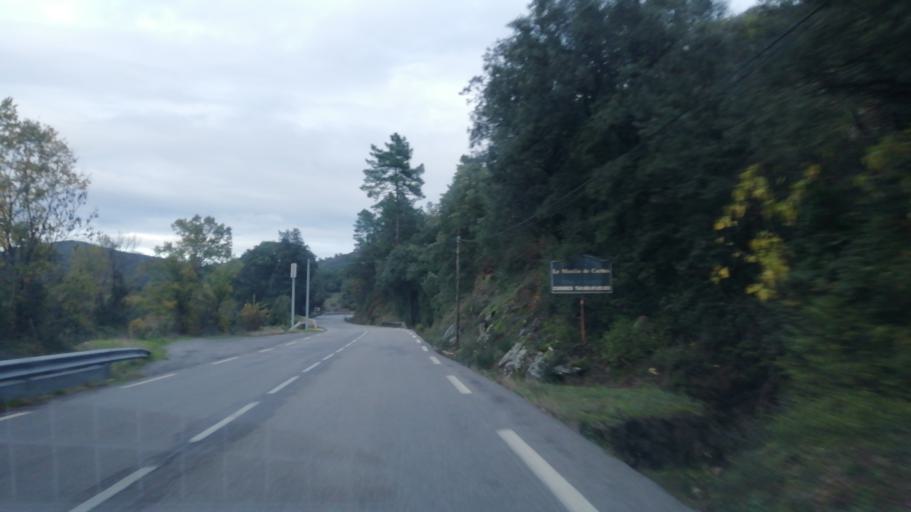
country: FR
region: Languedoc-Roussillon
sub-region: Departement du Gard
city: Anduze
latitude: 44.0727
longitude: 3.9605
